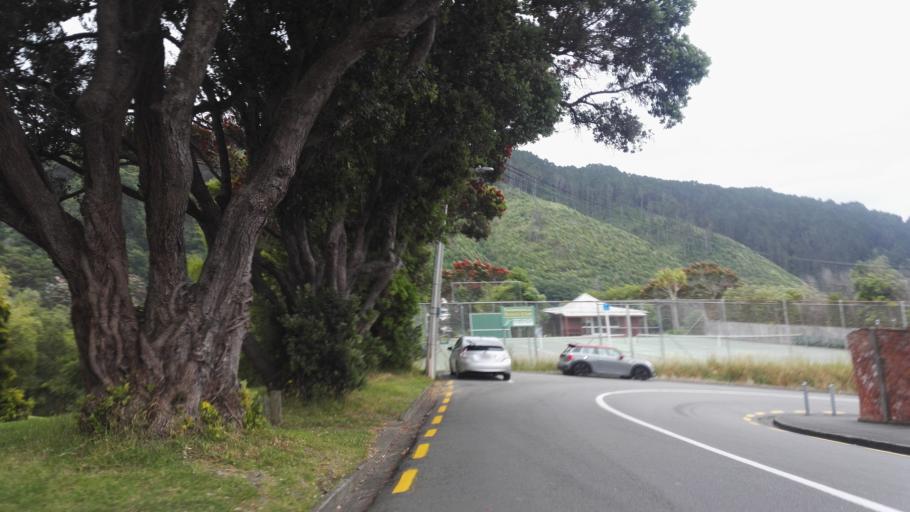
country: NZ
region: Wellington
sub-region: Wellington City
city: Kelburn
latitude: -41.2817
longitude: 174.7708
